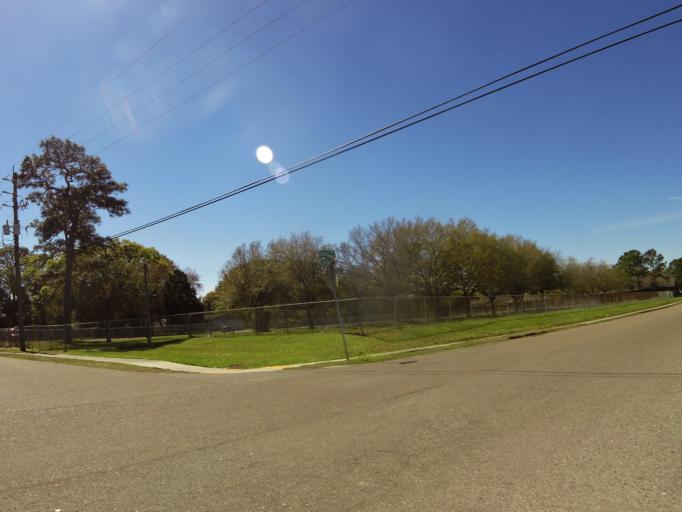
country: US
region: Florida
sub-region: Duval County
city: Jacksonville
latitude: 30.3246
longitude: -81.7191
